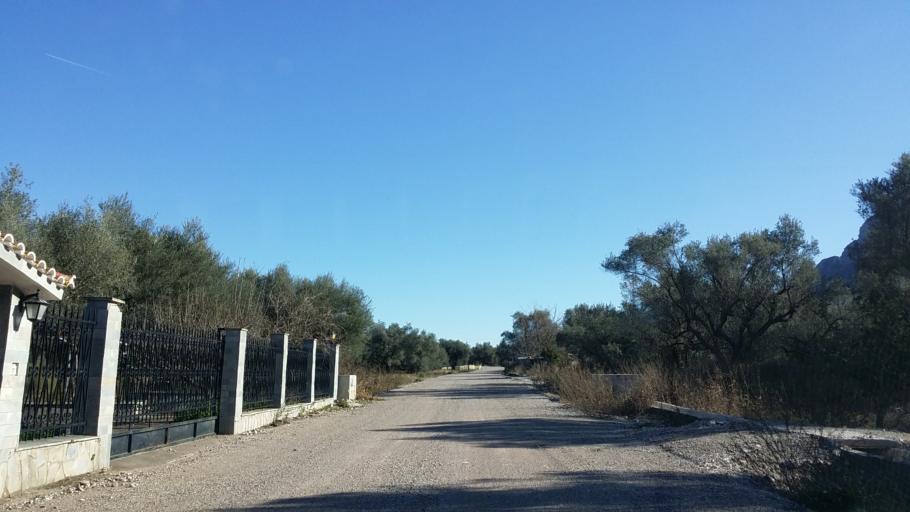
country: GR
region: West Greece
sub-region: Nomos Achaias
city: Temeni
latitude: 38.1933
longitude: 22.1823
